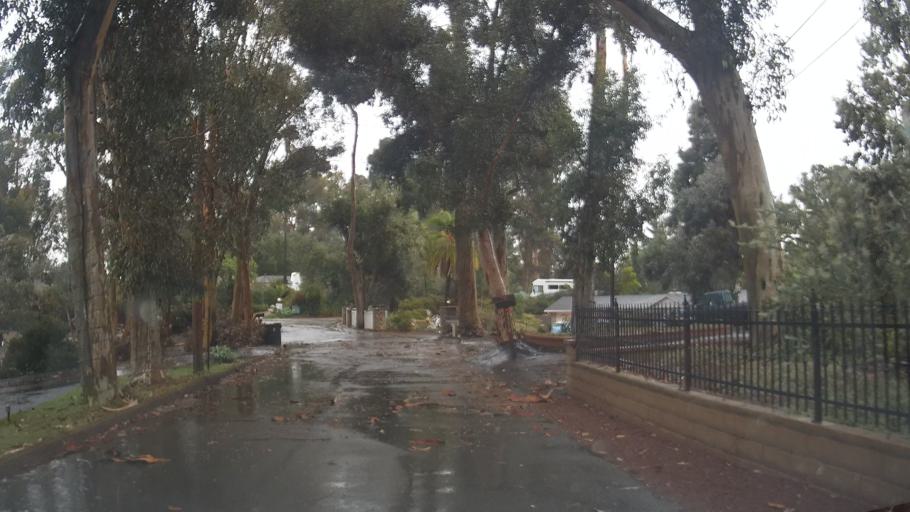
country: US
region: California
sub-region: San Diego County
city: Bonita
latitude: 32.6613
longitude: -117.0527
